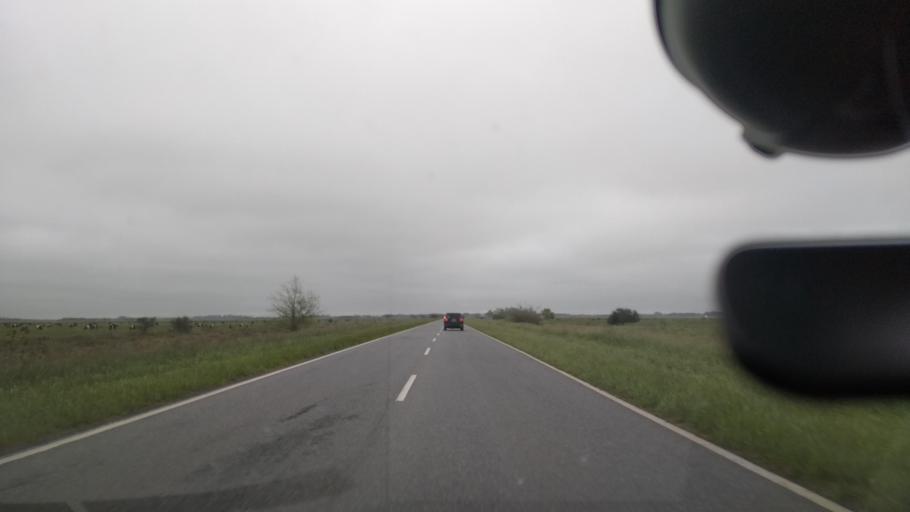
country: AR
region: Buenos Aires
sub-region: Partido de Magdalena
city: Magdalena
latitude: -35.2583
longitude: -57.6495
